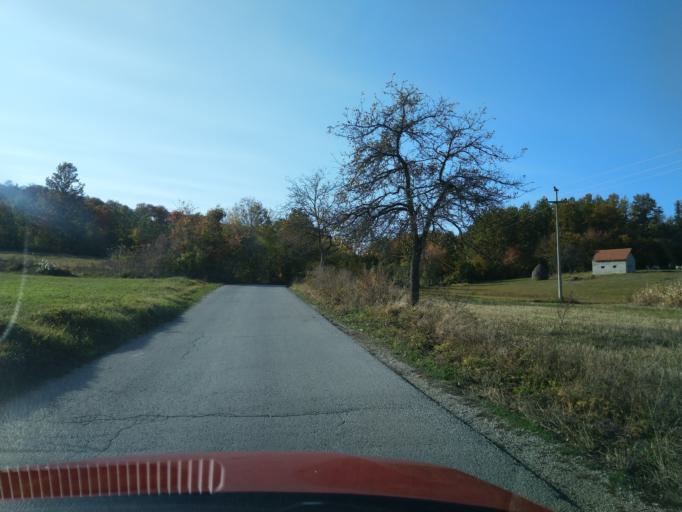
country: RS
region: Central Serbia
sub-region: Zlatiborski Okrug
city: Uzice
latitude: 43.8625
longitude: 19.7714
